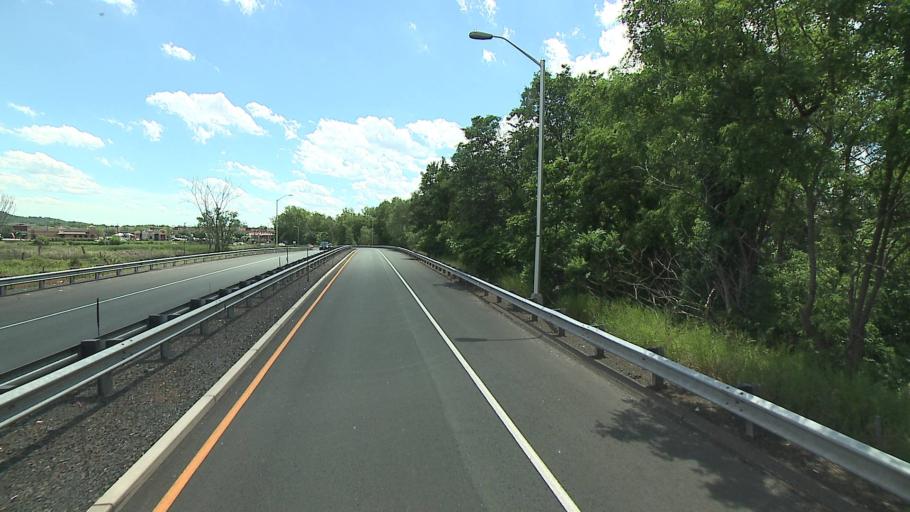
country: US
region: Connecticut
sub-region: Hartford County
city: Hartford
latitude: 41.7452
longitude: -72.7109
